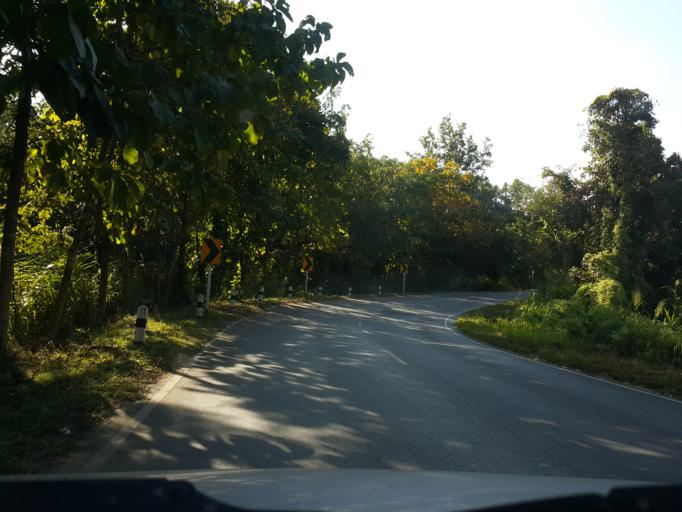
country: TH
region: Mae Hong Son
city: Mae Hi
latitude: 19.3040
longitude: 98.4575
